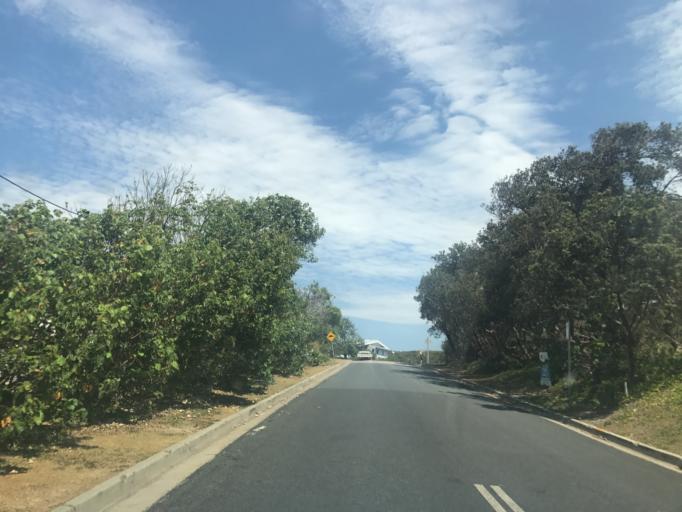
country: AU
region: Queensland
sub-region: Redland
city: Victoria Point
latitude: -27.4343
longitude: 153.5418
